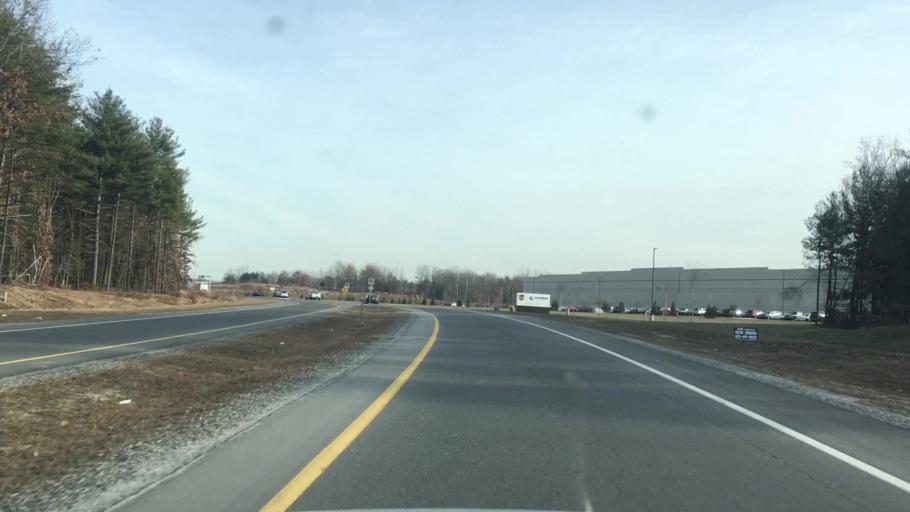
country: US
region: New Hampshire
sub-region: Hillsborough County
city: East Merrimack
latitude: 42.9152
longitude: -71.4424
